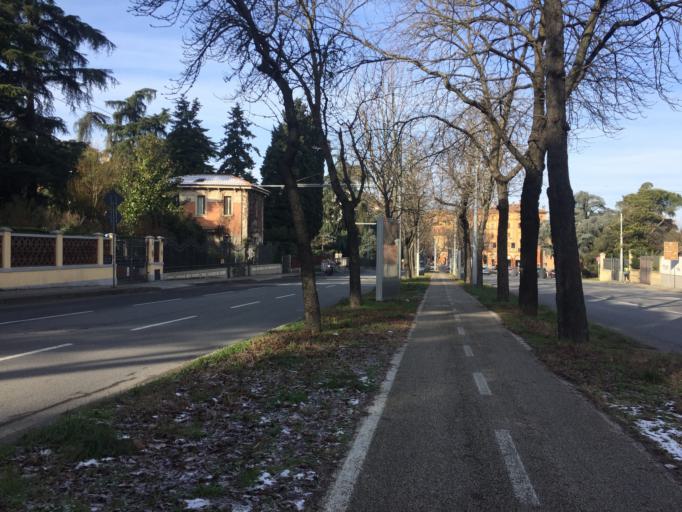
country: IT
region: Emilia-Romagna
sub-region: Provincia di Bologna
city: Bologna
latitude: 44.4895
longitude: 11.3315
